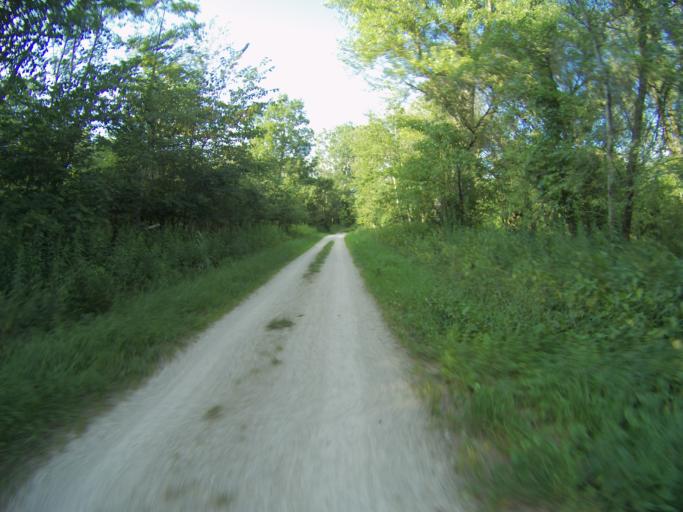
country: DE
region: Bavaria
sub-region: Upper Bavaria
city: Hallbergmoos
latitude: 48.3318
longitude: 11.7118
